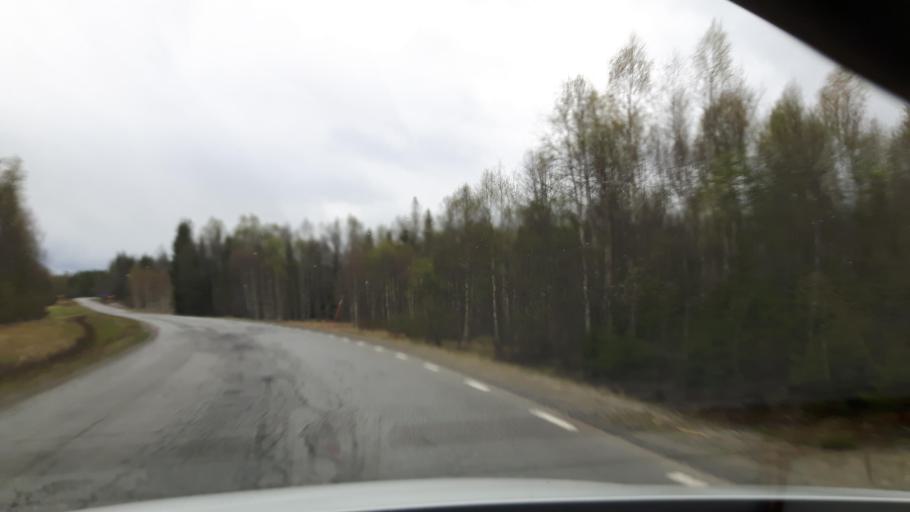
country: SE
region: Vaesterbotten
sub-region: Skelleftea Kommun
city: Burtraesk
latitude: 64.2742
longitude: 20.5380
